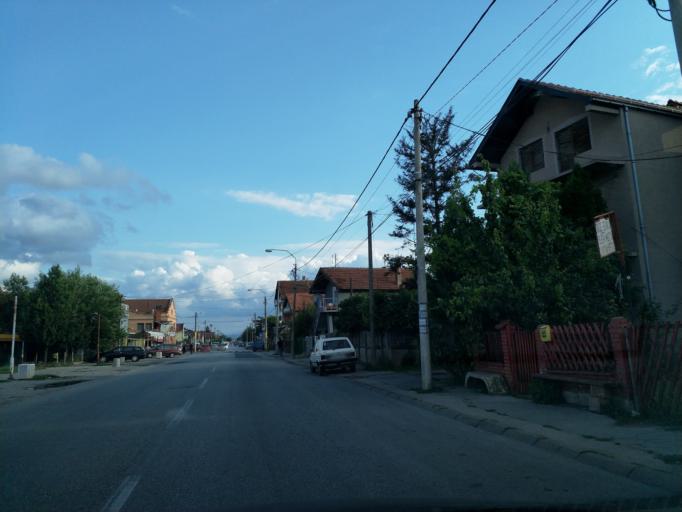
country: RS
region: Central Serbia
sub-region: Pomoravski Okrug
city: Paracin
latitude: 43.8517
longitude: 21.4132
